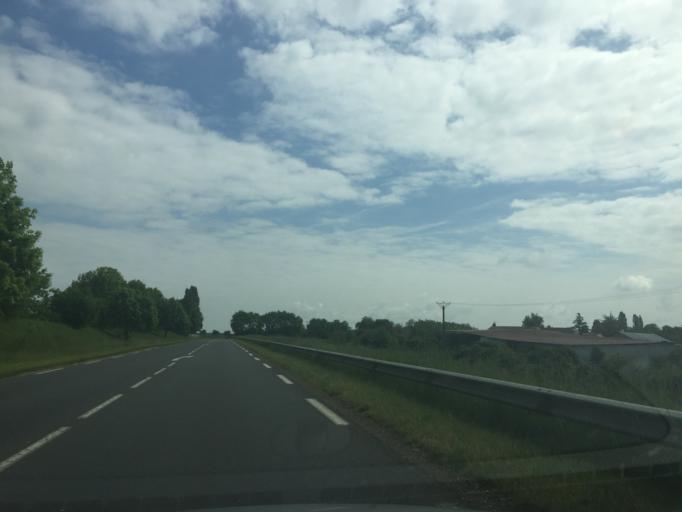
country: FR
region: Poitou-Charentes
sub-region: Departement de la Vienne
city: Lusignan
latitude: 46.4320
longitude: 0.1335
